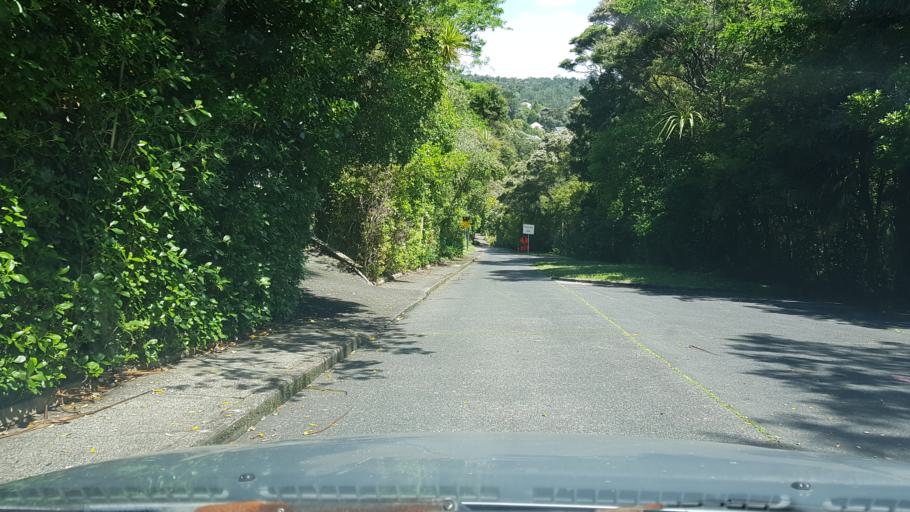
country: NZ
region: Auckland
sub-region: Auckland
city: North Shore
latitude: -36.8104
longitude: 174.7049
